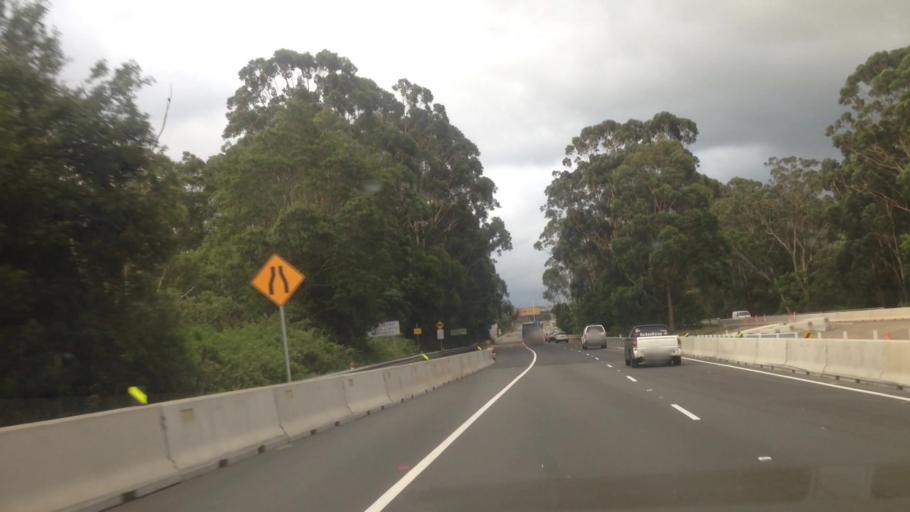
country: AU
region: New South Wales
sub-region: Wyong Shire
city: Little Jilliby
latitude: -33.2802
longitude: 151.4056
